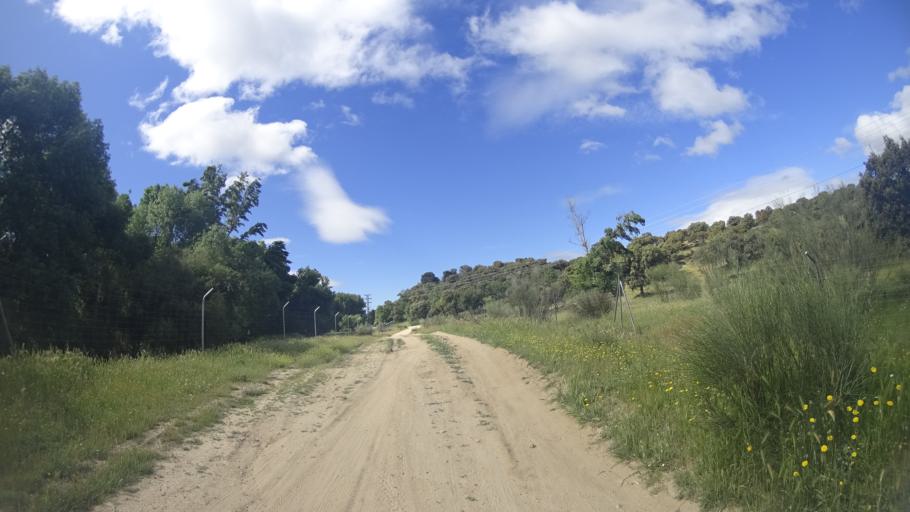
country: ES
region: Madrid
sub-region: Provincia de Madrid
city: Villanueva del Pardillo
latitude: 40.4358
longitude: -3.9523
